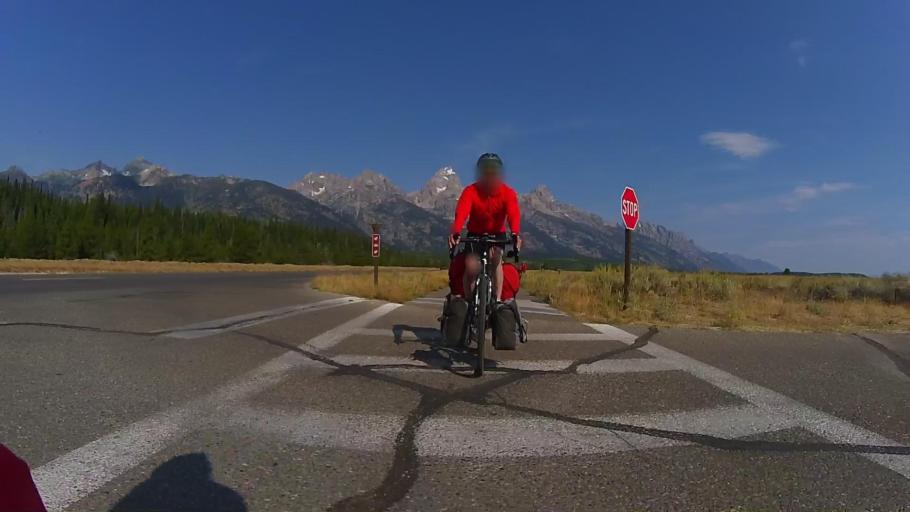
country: US
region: Wyoming
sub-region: Teton County
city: Moose Wilson Road
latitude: 43.6768
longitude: -110.7244
